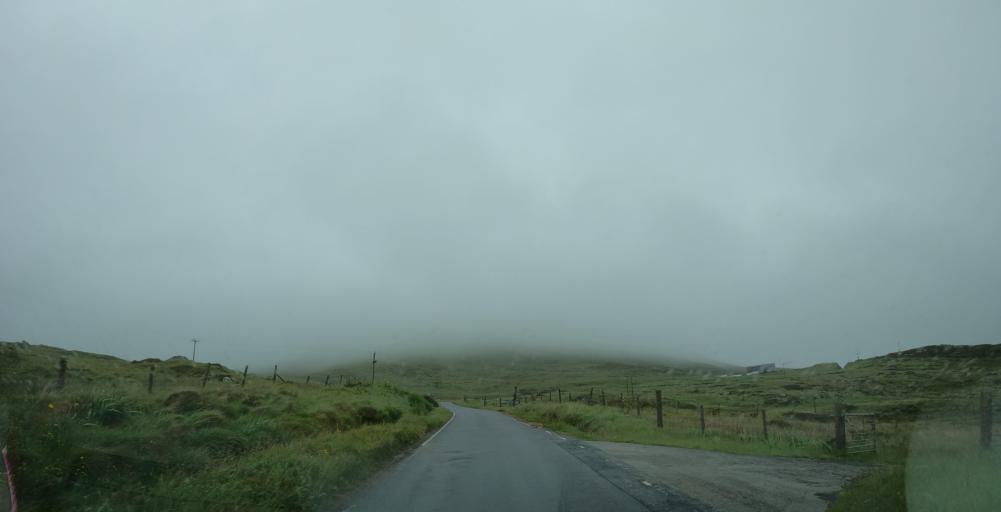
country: GB
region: Scotland
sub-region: Eilean Siar
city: Barra
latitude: 56.9583
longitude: -7.4705
